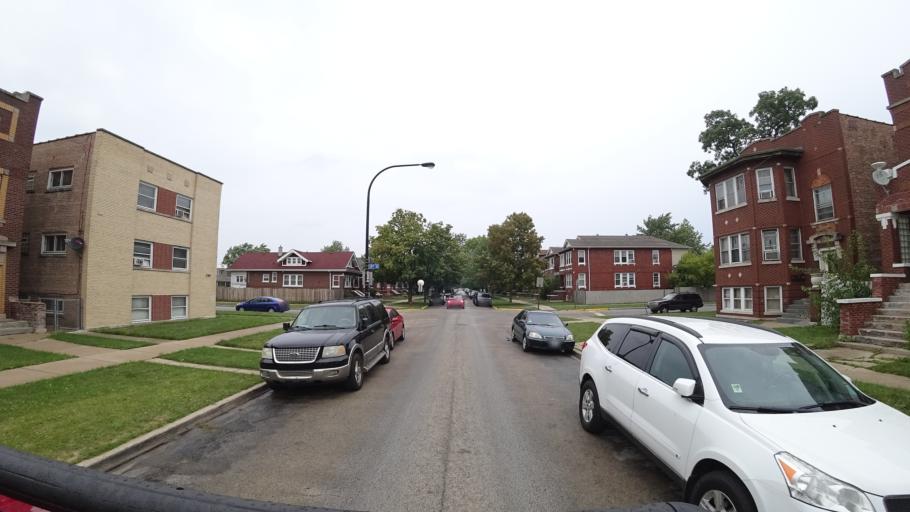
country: US
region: Illinois
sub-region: Cook County
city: Cicero
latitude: 41.8561
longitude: -87.7702
